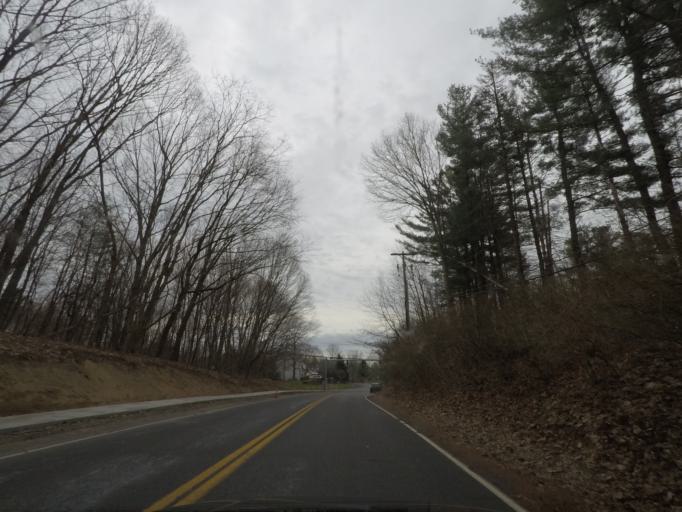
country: US
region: New York
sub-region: Albany County
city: Delmar
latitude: 42.6002
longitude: -73.8239
